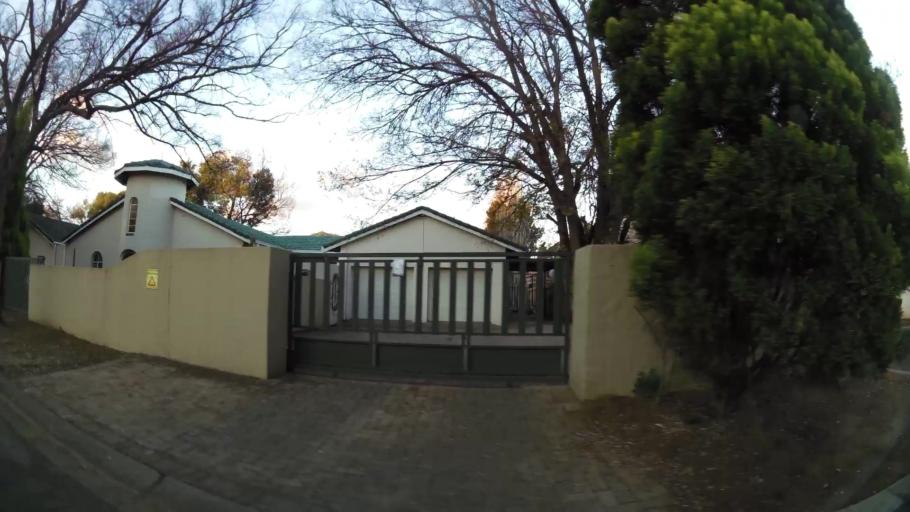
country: ZA
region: North-West
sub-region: Dr Kenneth Kaunda District Municipality
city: Potchefstroom
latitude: -26.7243
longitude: 27.1124
